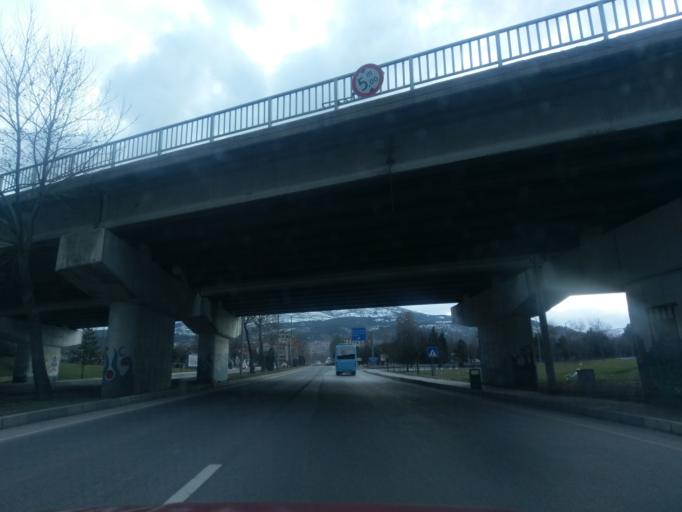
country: TR
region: Kuetahya
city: Kutahya
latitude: 39.4314
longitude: 29.9952
